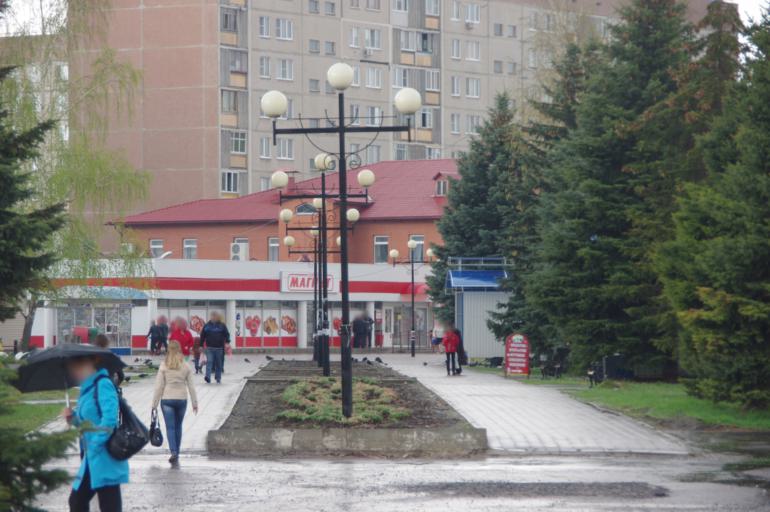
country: RU
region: Kursk
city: Kurchatov
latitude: 51.6552
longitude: 35.6838
